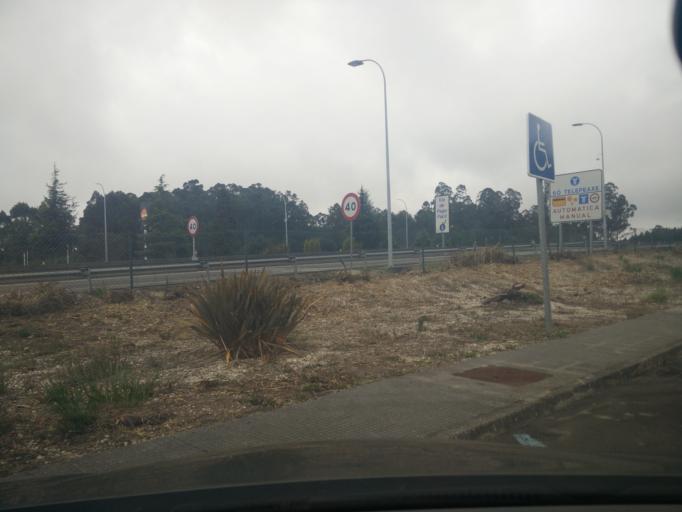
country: ES
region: Galicia
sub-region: Provincia da Coruna
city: Arteixo
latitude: 43.2750
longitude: -8.5286
